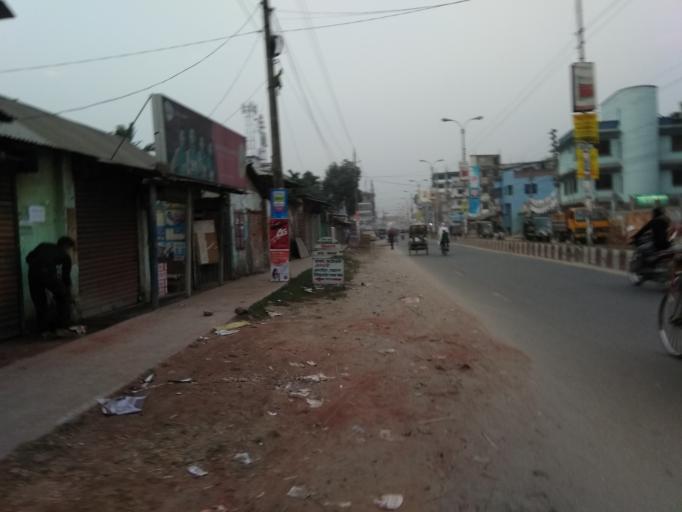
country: BD
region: Rangpur Division
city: Rangpur
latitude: 25.7310
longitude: 89.2547
